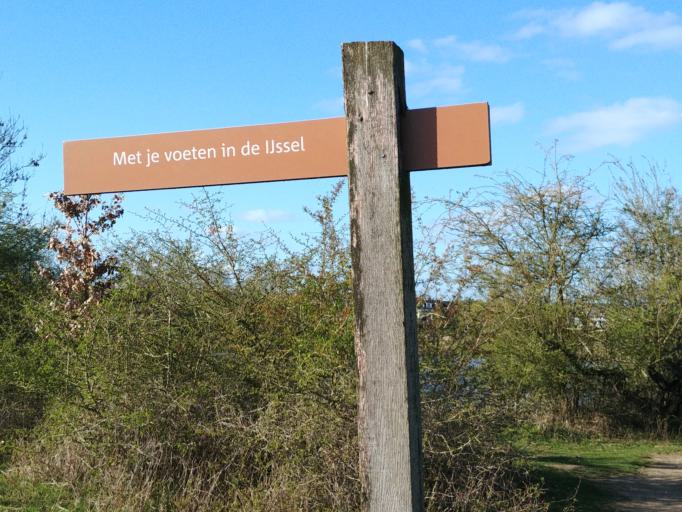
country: NL
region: Overijssel
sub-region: Gemeente Olst-Wijhe
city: Olst
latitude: 52.3721
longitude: 6.0897
